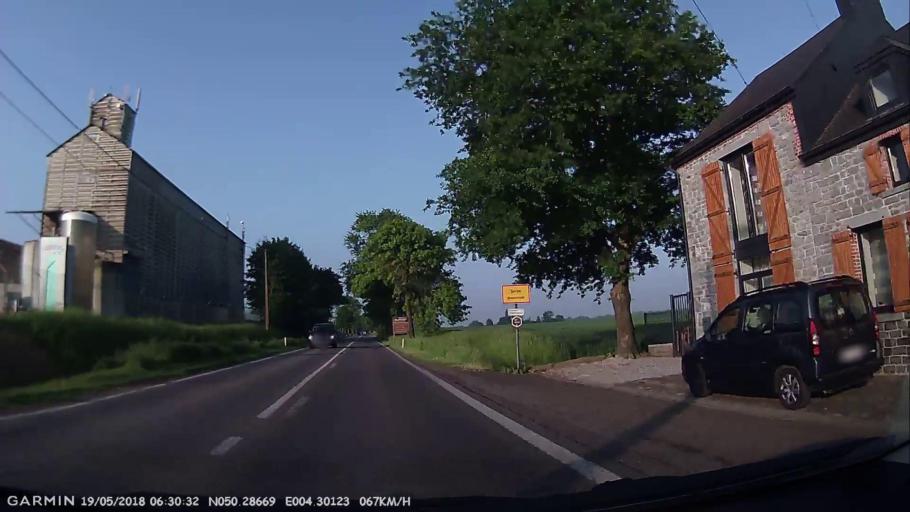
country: BE
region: Wallonia
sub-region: Province du Hainaut
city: Thuin
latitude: 50.2866
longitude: 4.3012
